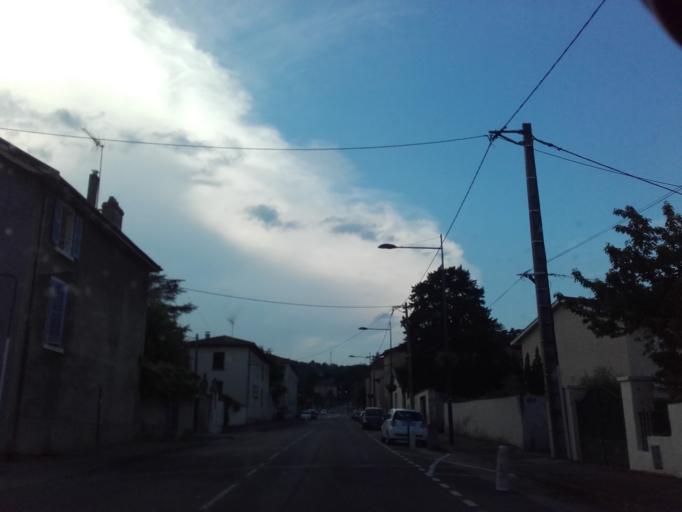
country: FR
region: Rhone-Alpes
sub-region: Departement du Rhone
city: Saint-Romain-en-Gal
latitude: 45.5418
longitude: 4.8683
